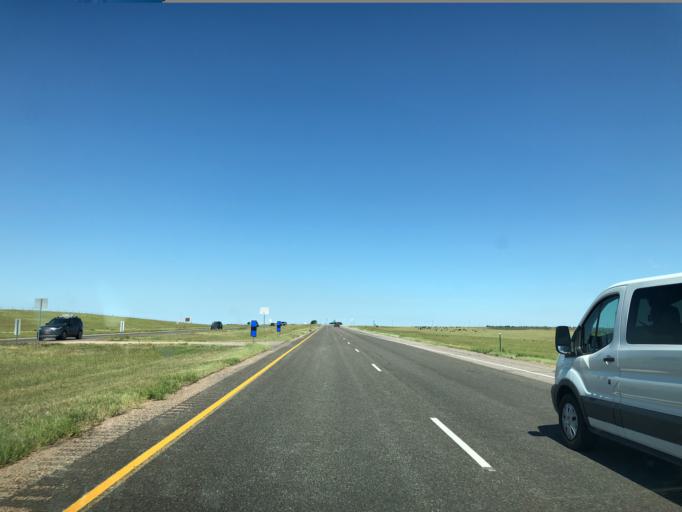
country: US
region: Colorado
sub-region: Lincoln County
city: Hugo
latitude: 39.2868
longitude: -103.0701
